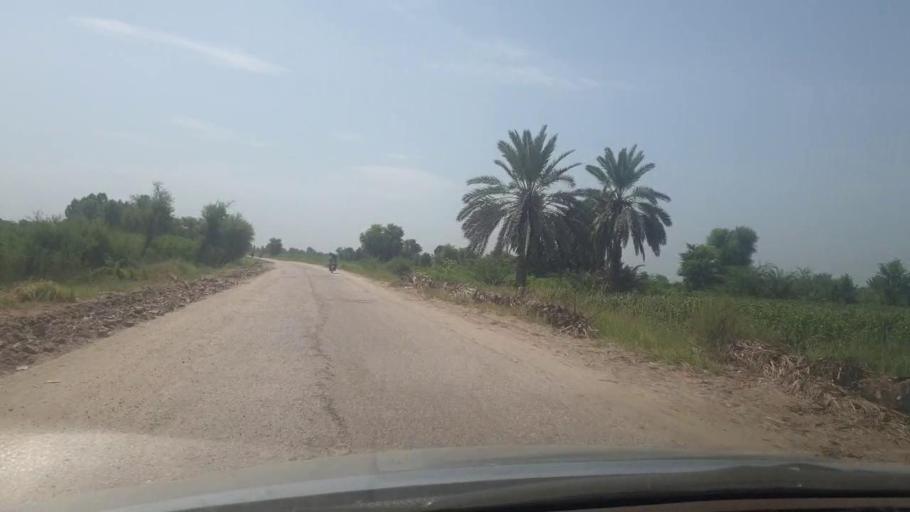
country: PK
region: Sindh
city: Bozdar
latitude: 27.2201
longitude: 68.5676
